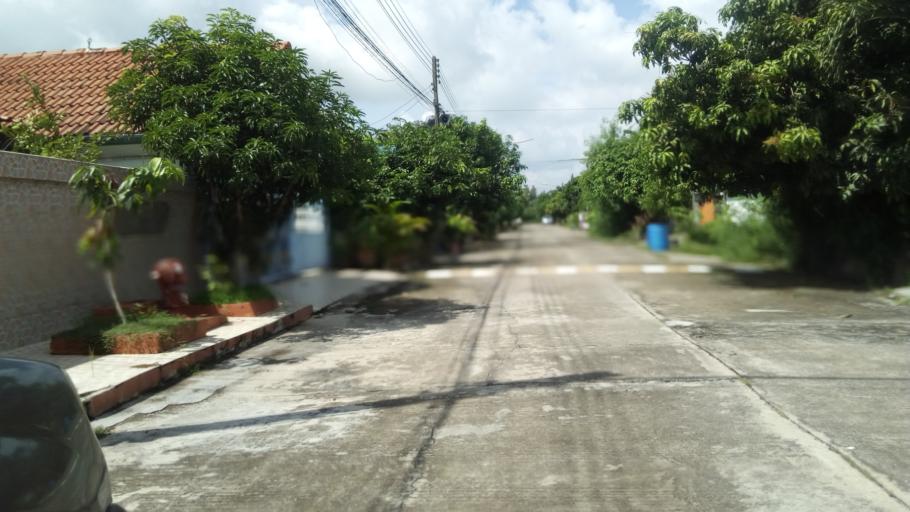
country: TH
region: Pathum Thani
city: Nong Suea
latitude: 14.0518
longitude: 100.8625
